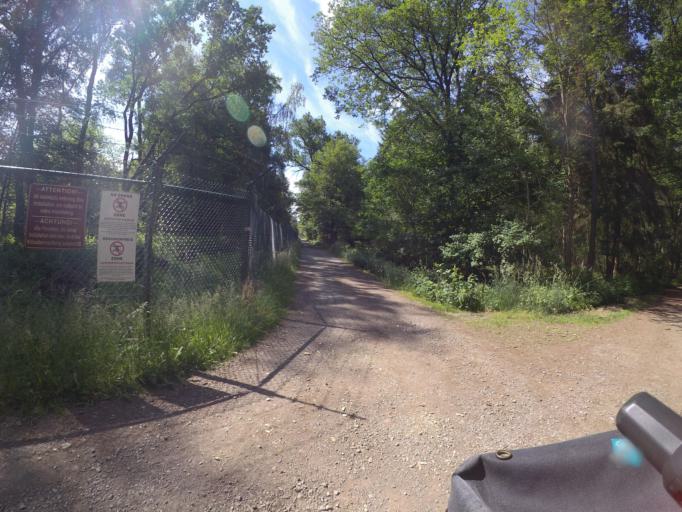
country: DE
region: Rheinland-Pfalz
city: Landstuhl
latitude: 49.4282
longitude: 7.5686
